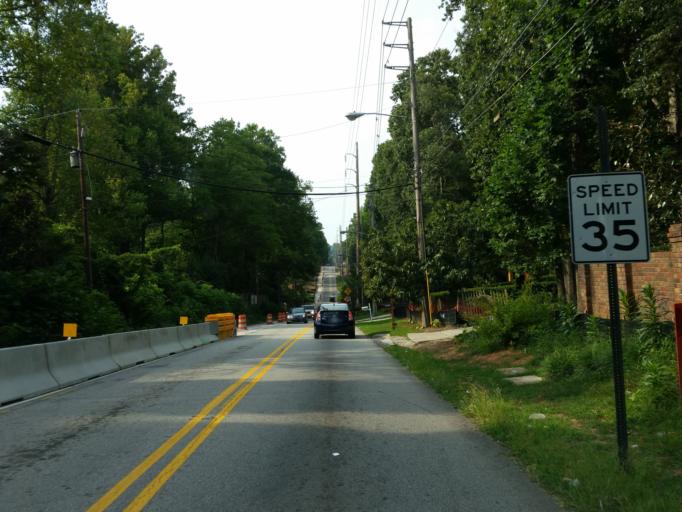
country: US
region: Georgia
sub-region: Fulton County
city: Atlanta
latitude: 33.8105
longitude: -84.4077
